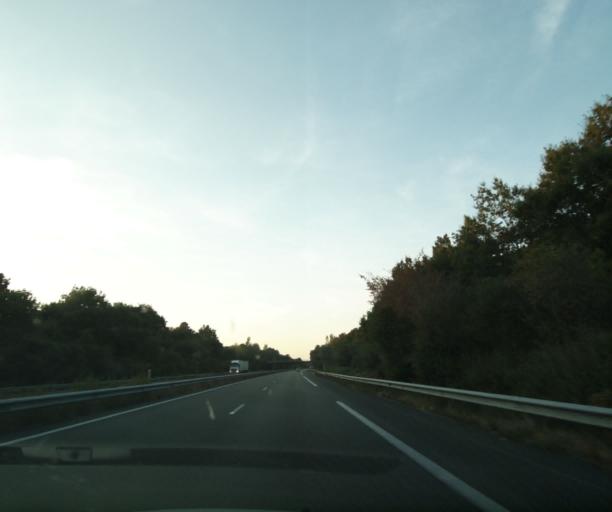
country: FR
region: Aquitaine
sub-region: Departement du Lot-et-Garonne
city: Fourques-sur-Garonne
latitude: 44.3895
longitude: 0.1980
